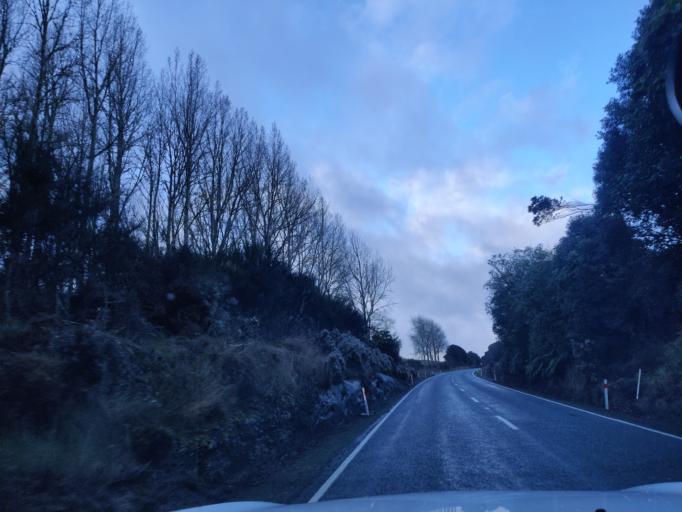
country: NZ
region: Waikato
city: Turangi
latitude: -38.7157
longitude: 175.6608
